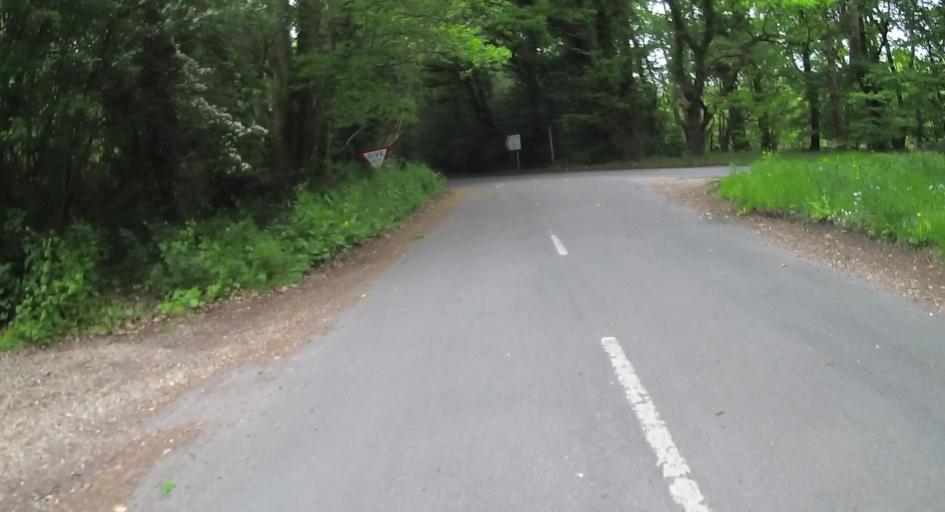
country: GB
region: England
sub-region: Hampshire
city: Eversley
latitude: 51.3450
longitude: -0.9218
